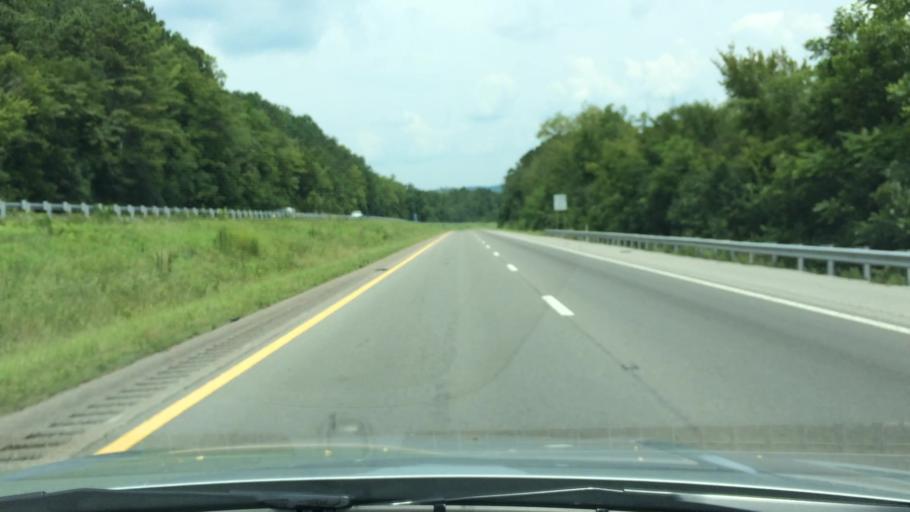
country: US
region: Tennessee
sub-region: Marshall County
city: Cornersville
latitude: 35.2646
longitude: -86.8867
